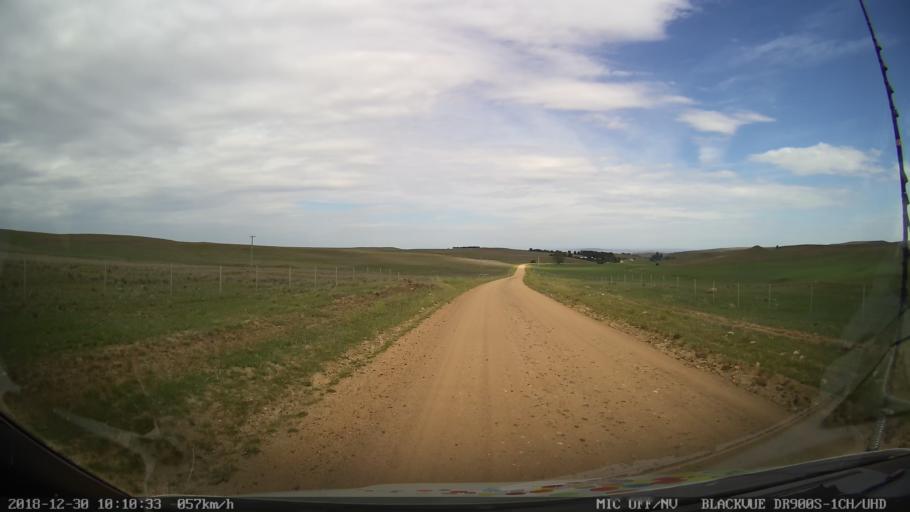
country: AU
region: New South Wales
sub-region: Cooma-Monaro
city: Cooma
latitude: -36.5509
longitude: 149.0937
